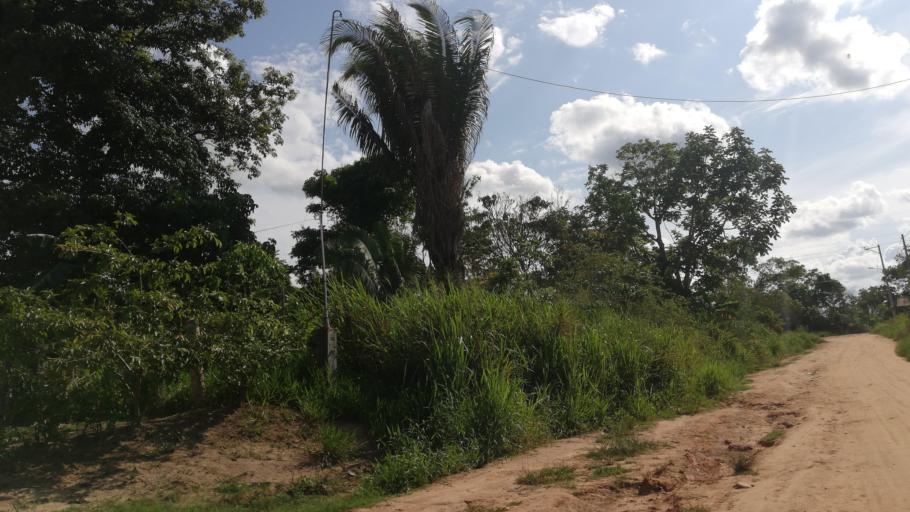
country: PE
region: Ucayali
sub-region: Provincia de Coronel Portillo
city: Puerto Callao
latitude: -8.2693
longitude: -74.6475
